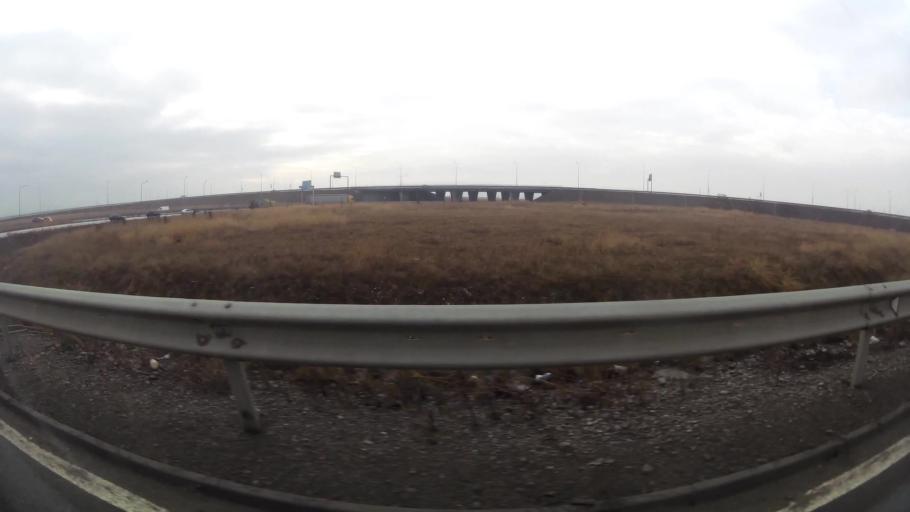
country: BG
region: Sofia-Capital
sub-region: Stolichna Obshtina
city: Sofia
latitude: 42.7707
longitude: 23.2874
